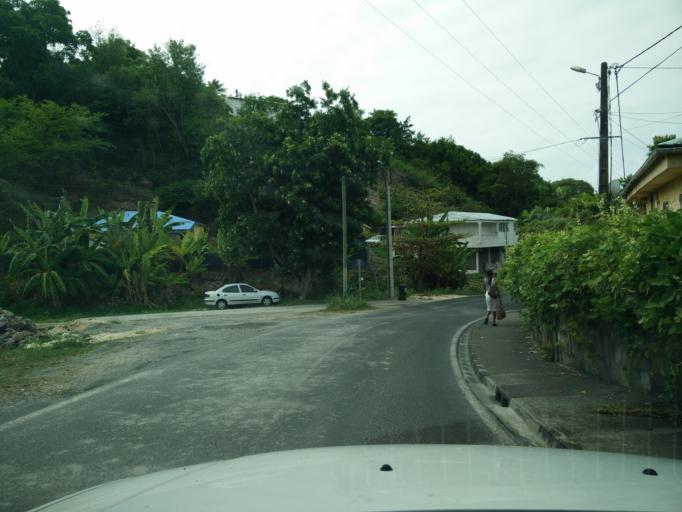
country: GP
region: Guadeloupe
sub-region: Guadeloupe
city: Le Gosier
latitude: 16.2111
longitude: -61.4655
